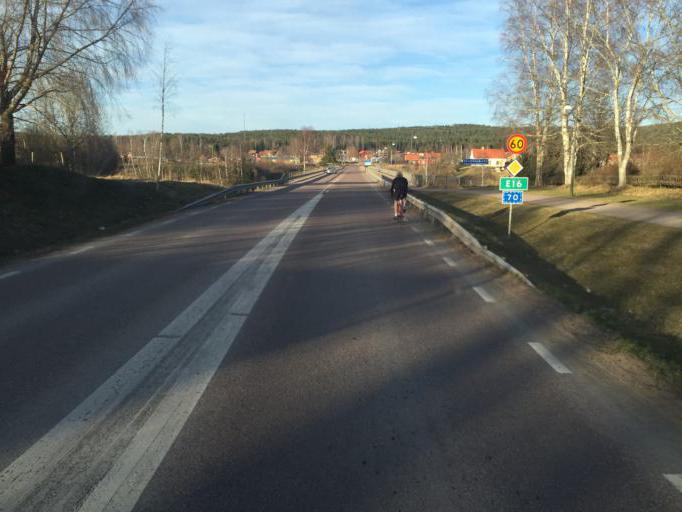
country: SE
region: Dalarna
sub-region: Gagnefs Kommun
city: Djuras
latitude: 60.5576
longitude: 15.1228
